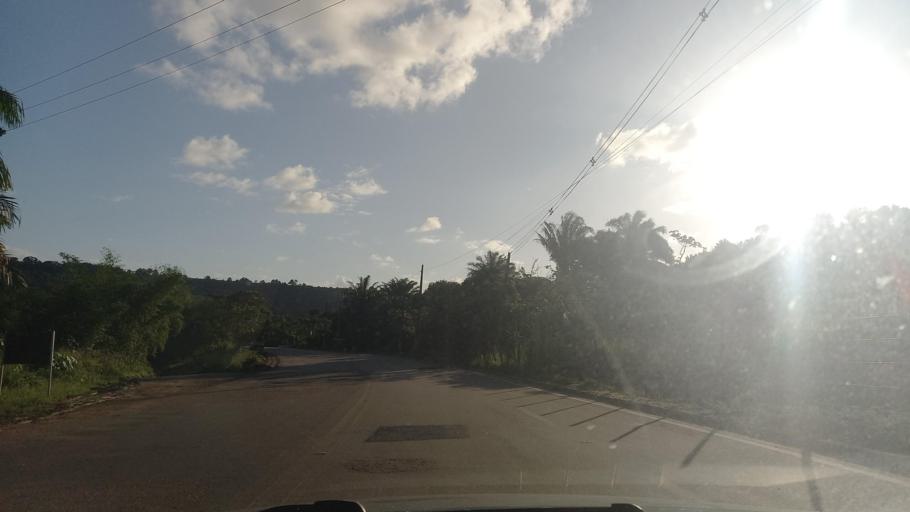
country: BR
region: Alagoas
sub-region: Sao Miguel Dos Campos
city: Sao Miguel dos Campos
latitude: -9.8089
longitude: -36.2182
